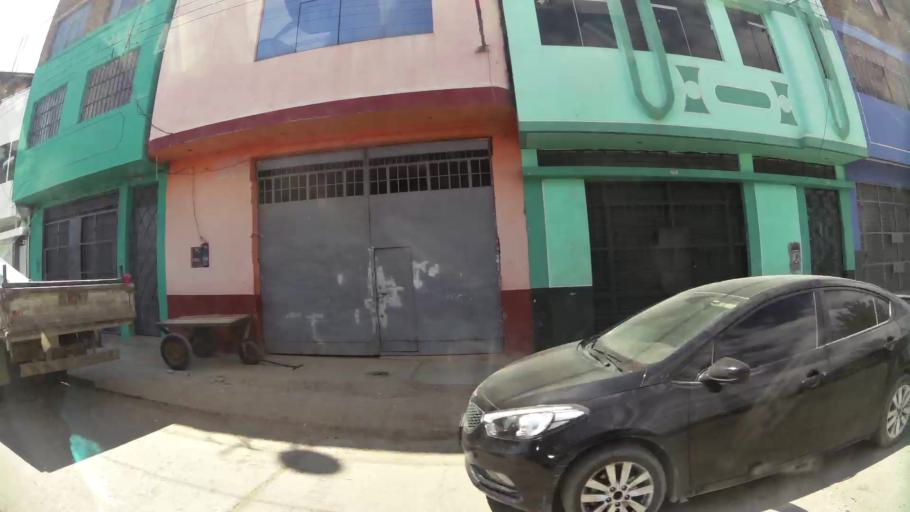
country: PE
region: Junin
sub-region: Provincia de Huancayo
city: El Tambo
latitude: -12.0779
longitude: -75.2101
